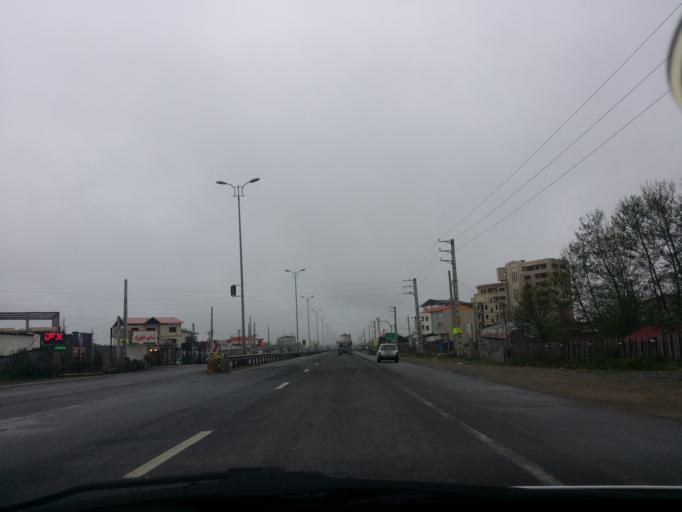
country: IR
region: Mazandaran
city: Tonekabon
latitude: 36.7959
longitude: 50.9119
